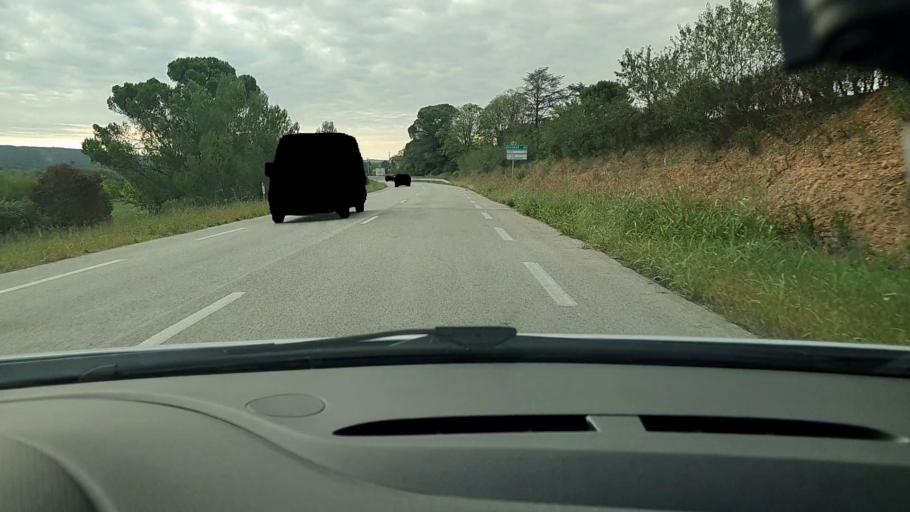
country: FR
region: Languedoc-Roussillon
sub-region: Departement du Gard
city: Mons
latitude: 44.0737
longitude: 4.2201
